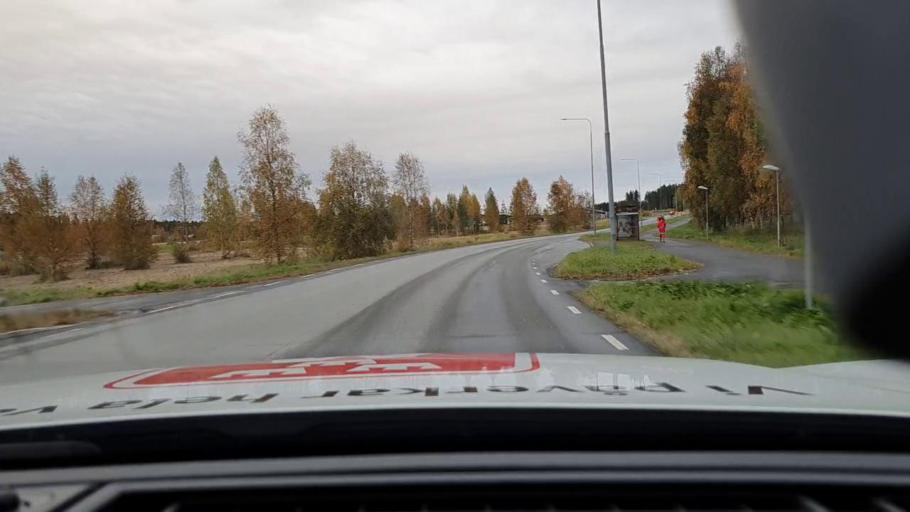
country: SE
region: Norrbotten
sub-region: Bodens Kommun
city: Saevast
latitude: 65.7571
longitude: 21.7550
